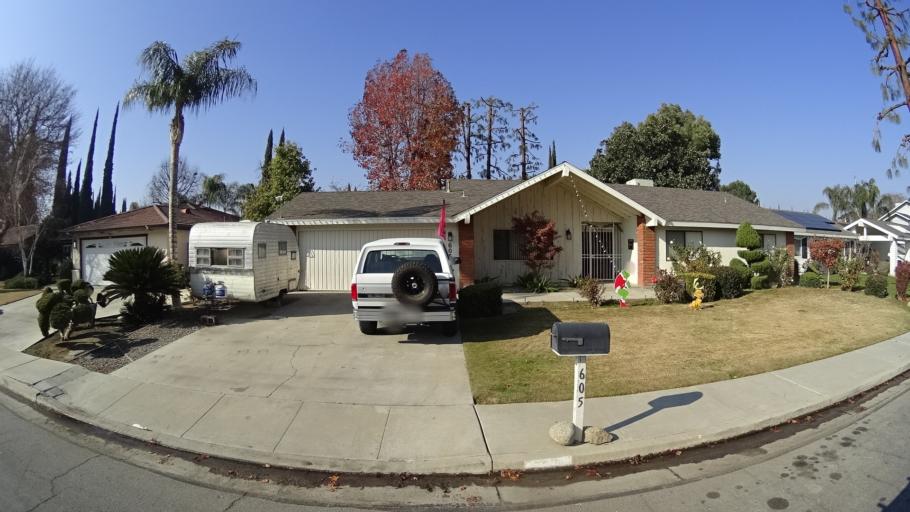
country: US
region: California
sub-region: Kern County
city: Greenacres
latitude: 35.3586
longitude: -119.0798
